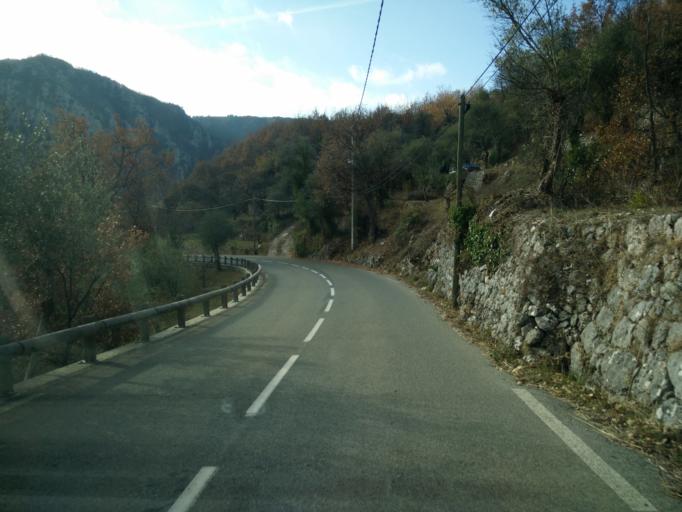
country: FR
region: Provence-Alpes-Cote d'Azur
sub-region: Departement des Alpes-Maritimes
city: Gilette
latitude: 43.8230
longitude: 7.1221
